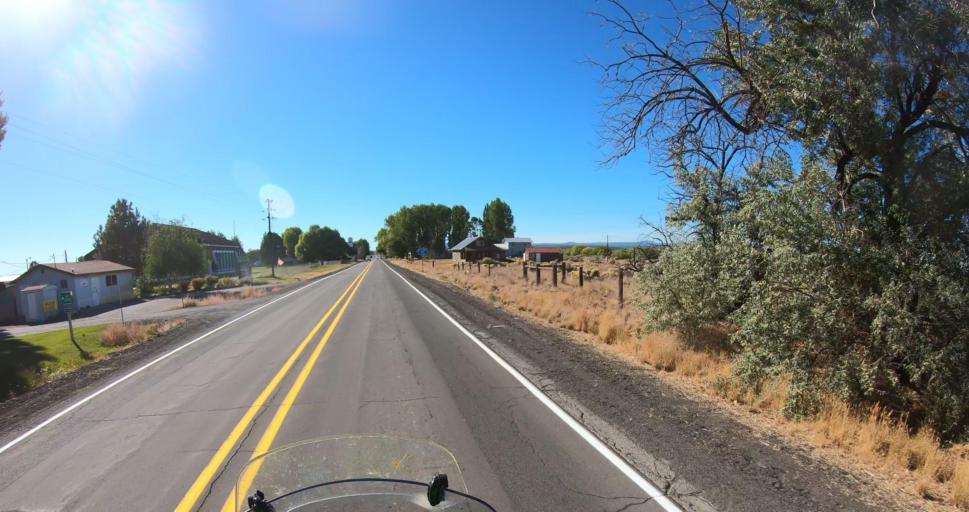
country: US
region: Oregon
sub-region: Deschutes County
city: La Pine
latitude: 43.1279
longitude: -121.0425
